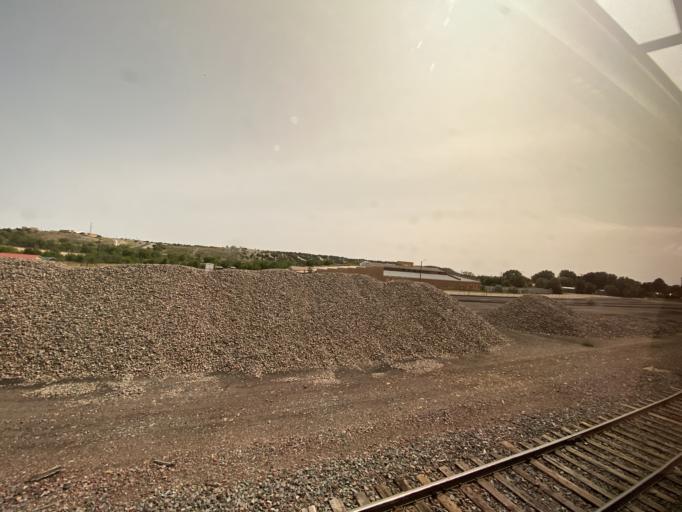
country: US
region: New Mexico
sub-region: San Miguel County
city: Las Vegas
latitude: 35.5936
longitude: -105.2123
